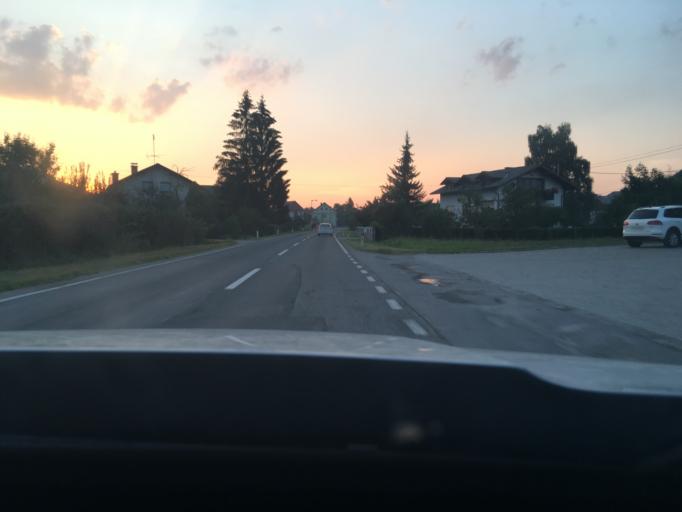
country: SI
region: Ribnica
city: Ribnica
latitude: 45.7118
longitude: 14.7511
